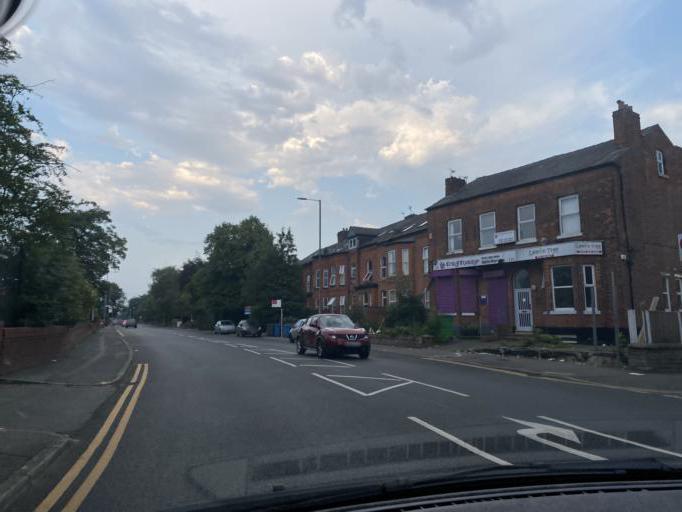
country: GB
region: England
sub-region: Manchester
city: Fallowfield
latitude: 53.4528
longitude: -2.2166
